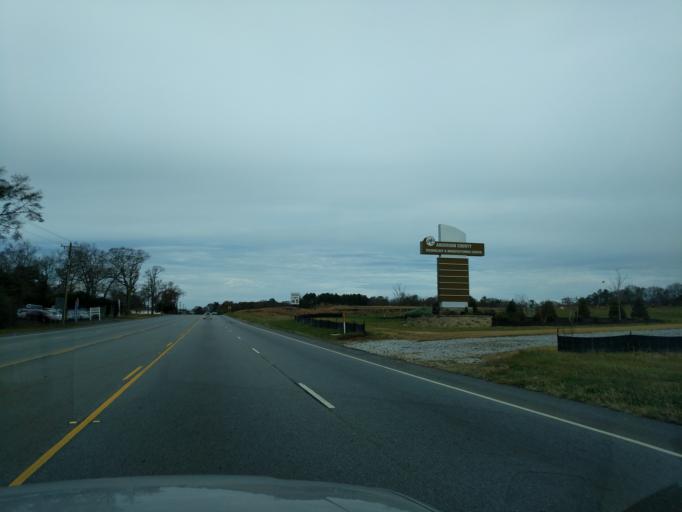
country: US
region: South Carolina
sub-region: Anderson County
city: Northlake
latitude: 34.5894
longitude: -82.7444
